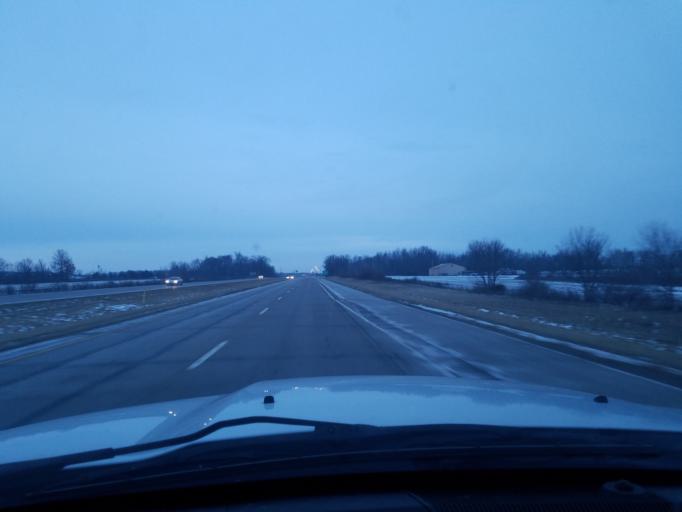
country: US
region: Indiana
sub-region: Delaware County
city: Muncie
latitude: 40.2031
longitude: -85.3363
